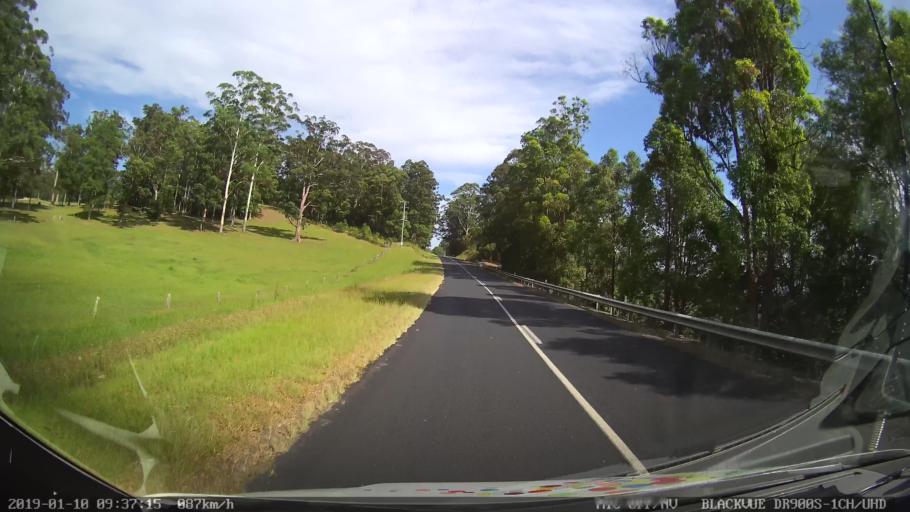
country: AU
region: New South Wales
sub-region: Coffs Harbour
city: Nana Glen
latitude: -30.1895
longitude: 153.0110
